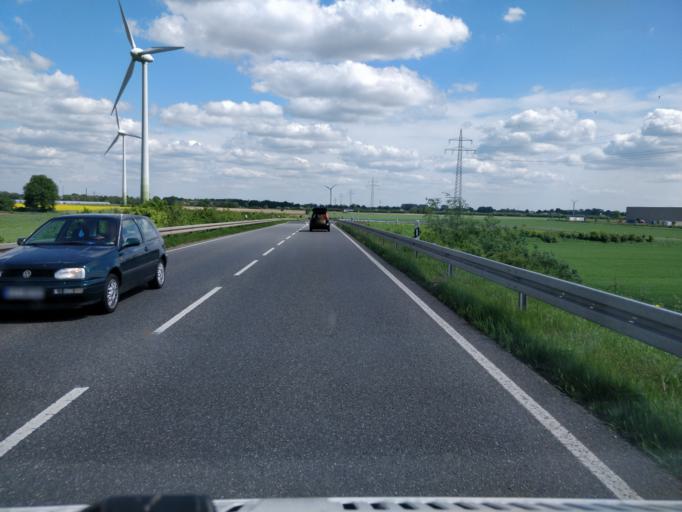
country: DE
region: North Rhine-Westphalia
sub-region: Regierungsbezirk Dusseldorf
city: Kleve
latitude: 51.8184
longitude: 6.1455
